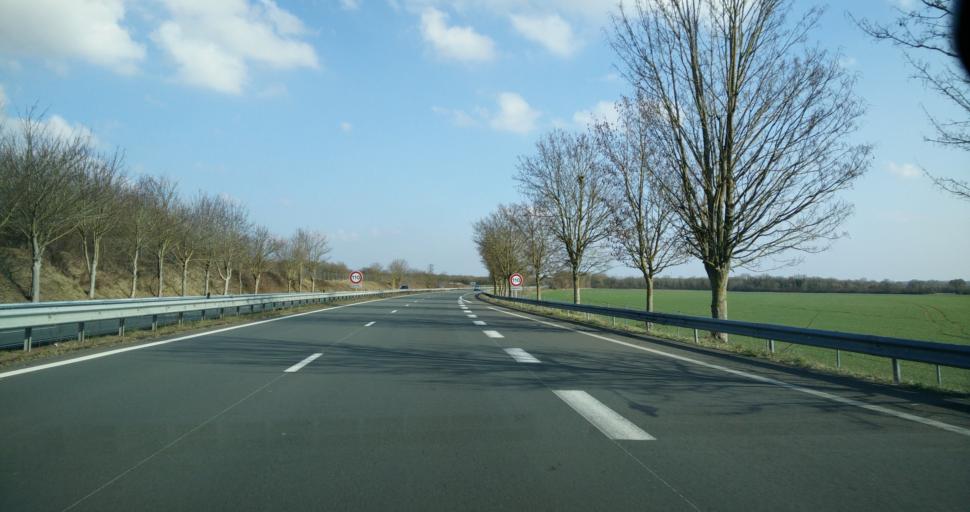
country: FR
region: Poitou-Charentes
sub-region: Departement de la Charente-Maritime
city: Courcon
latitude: 46.2245
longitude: -0.8422
